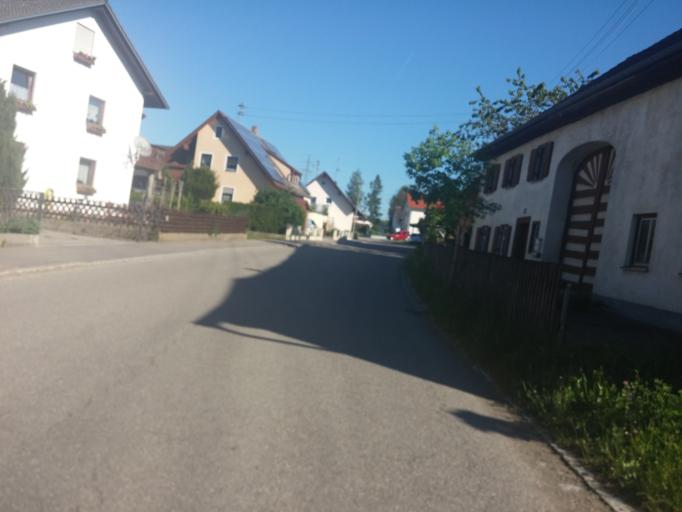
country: DE
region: Bavaria
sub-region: Swabia
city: Kronburg
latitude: 47.8955
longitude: 10.1442
